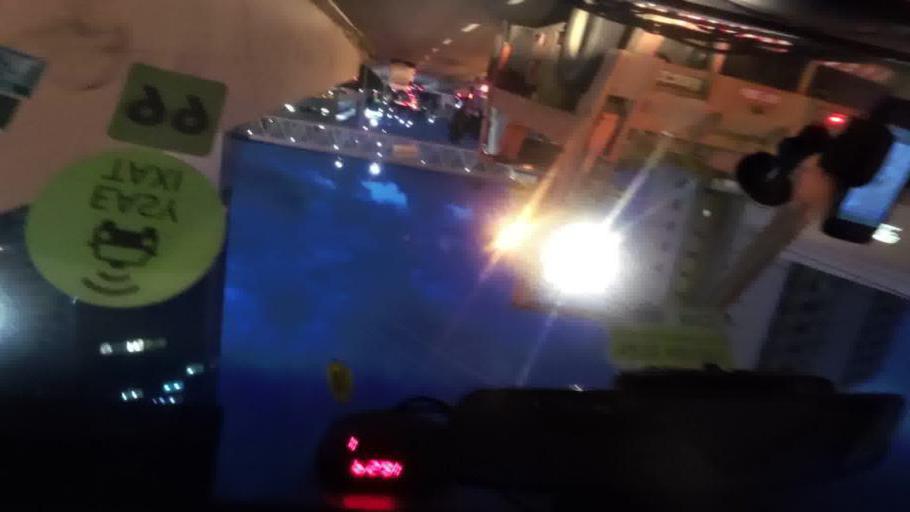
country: BR
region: Pernambuco
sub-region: Recife
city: Recife
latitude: -8.0867
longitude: -34.8908
